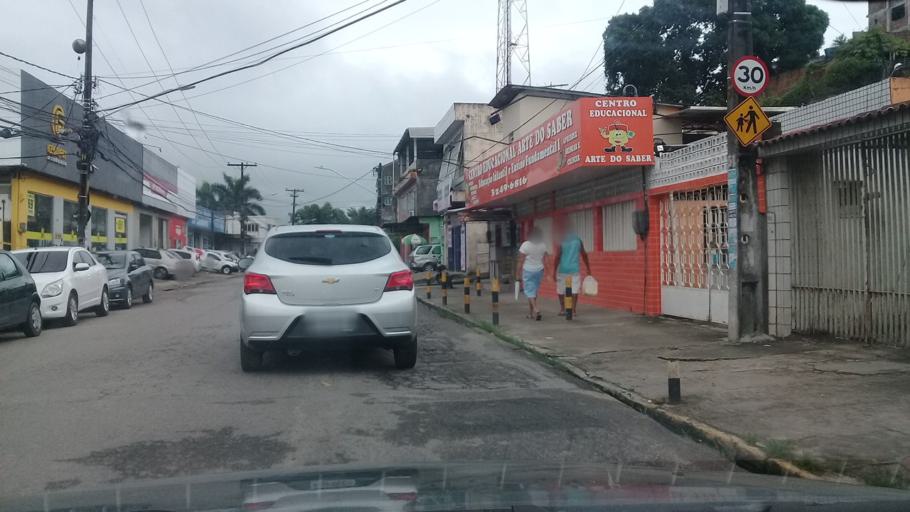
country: BR
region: Pernambuco
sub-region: Jaboatao Dos Guararapes
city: Jaboatao dos Guararapes
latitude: -8.0970
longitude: -34.9721
